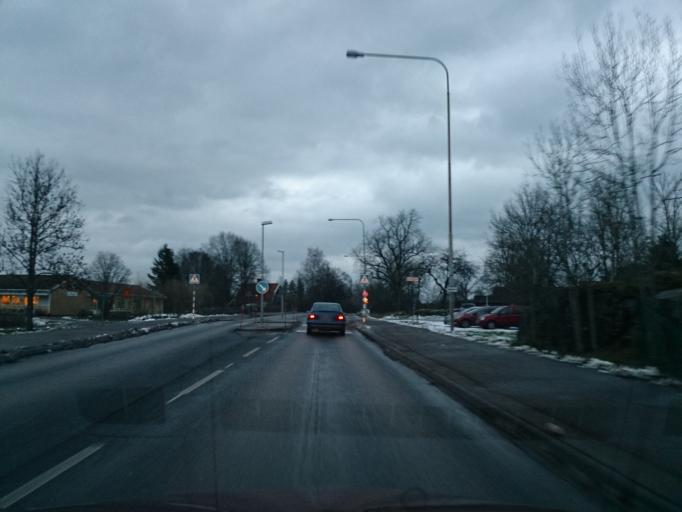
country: SE
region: OEstergoetland
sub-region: Linkopings Kommun
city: Sturefors
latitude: 58.3757
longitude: 15.7134
